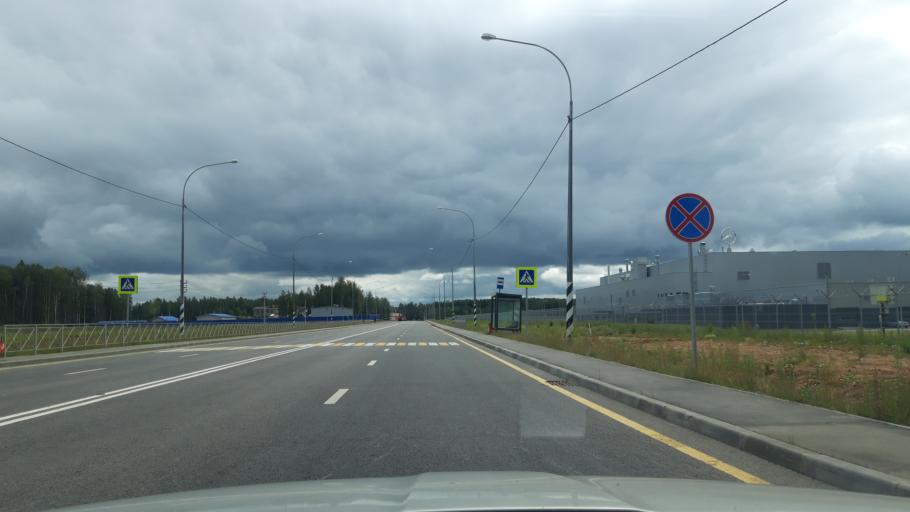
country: RU
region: Moskovskaya
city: Lozhki
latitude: 56.0861
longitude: 37.0823
